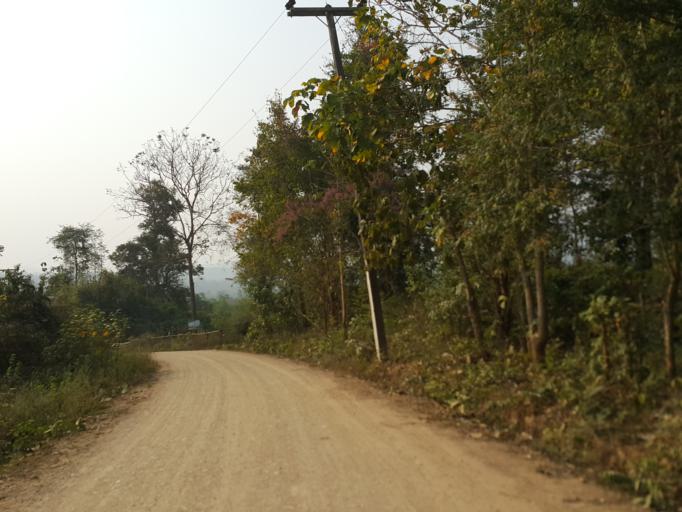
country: TH
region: Lamphun
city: Li
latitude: 17.6051
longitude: 98.9703
